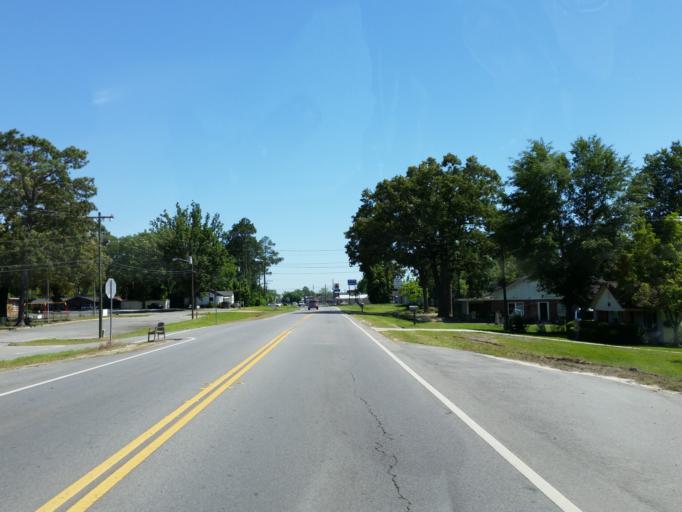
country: US
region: Georgia
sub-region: Cook County
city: Adel
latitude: 31.1503
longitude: -83.4279
